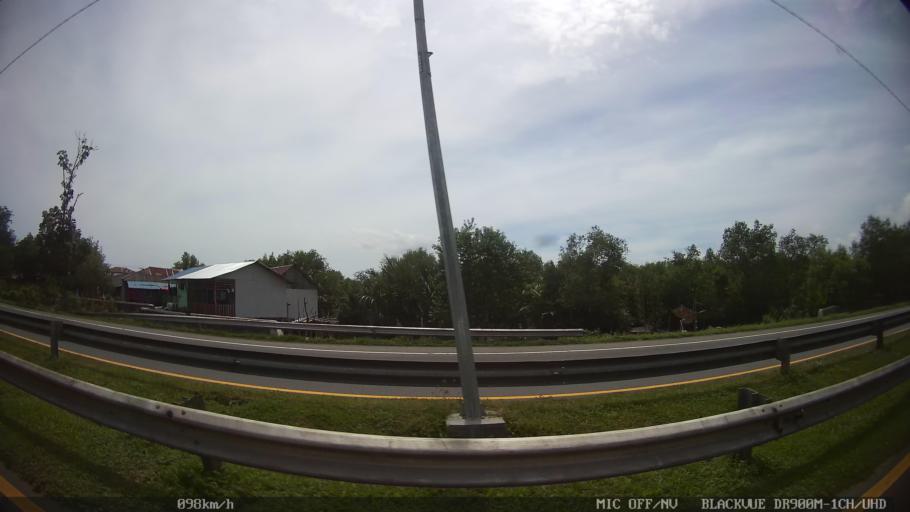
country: ID
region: North Sumatra
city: Labuhan Deli
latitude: 3.7401
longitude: 98.6794
